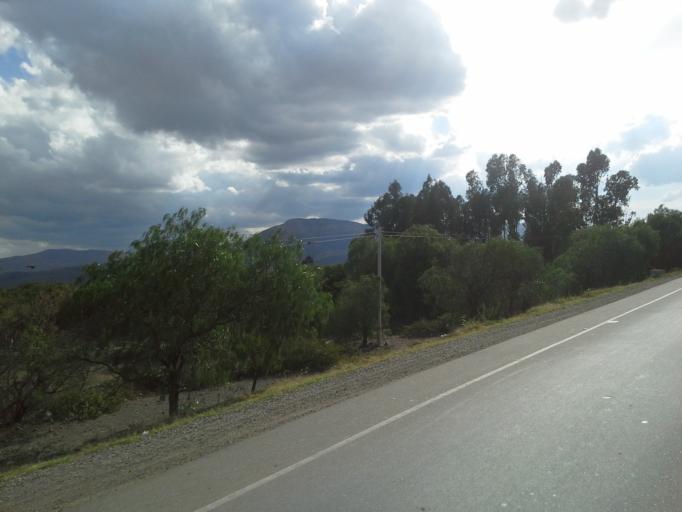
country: BO
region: Cochabamba
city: Tarata
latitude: -17.5442
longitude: -66.0228
